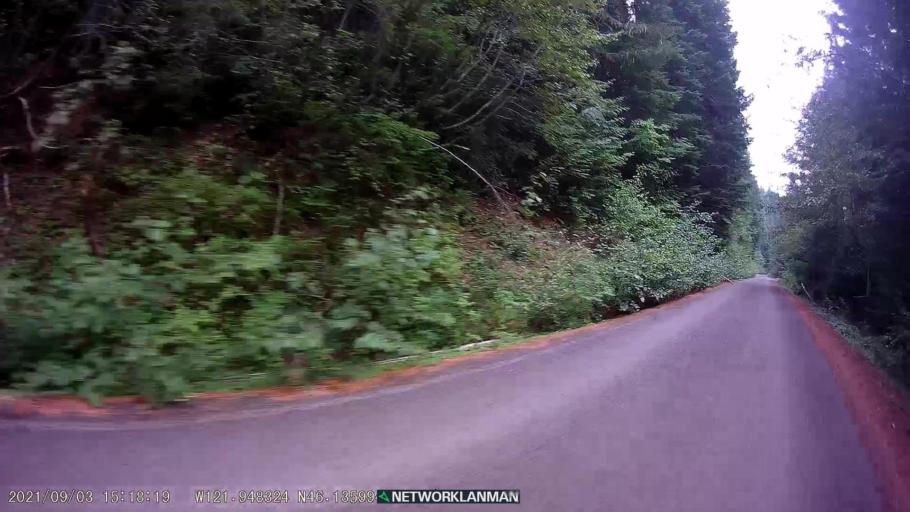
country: US
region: Washington
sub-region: Skamania County
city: Carson
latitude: 46.1359
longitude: -121.9485
